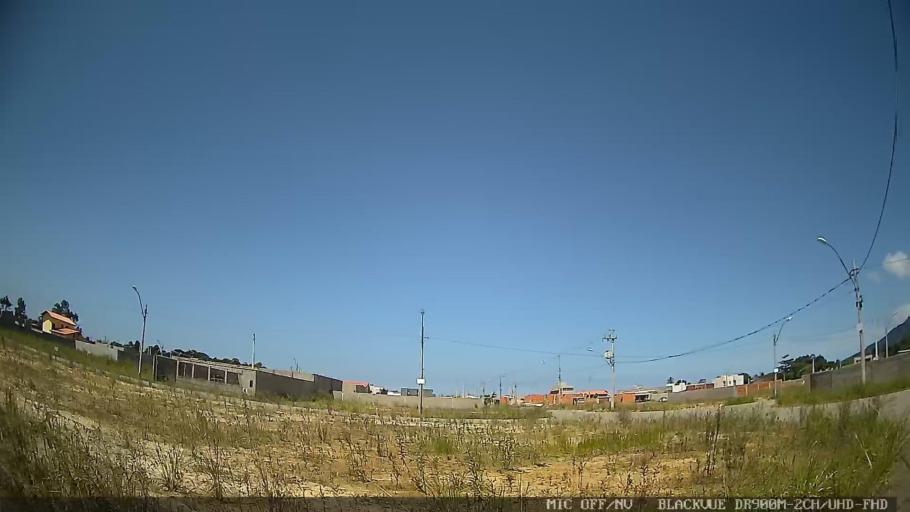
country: BR
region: Sao Paulo
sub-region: Peruibe
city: Peruibe
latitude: -24.2964
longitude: -47.0030
